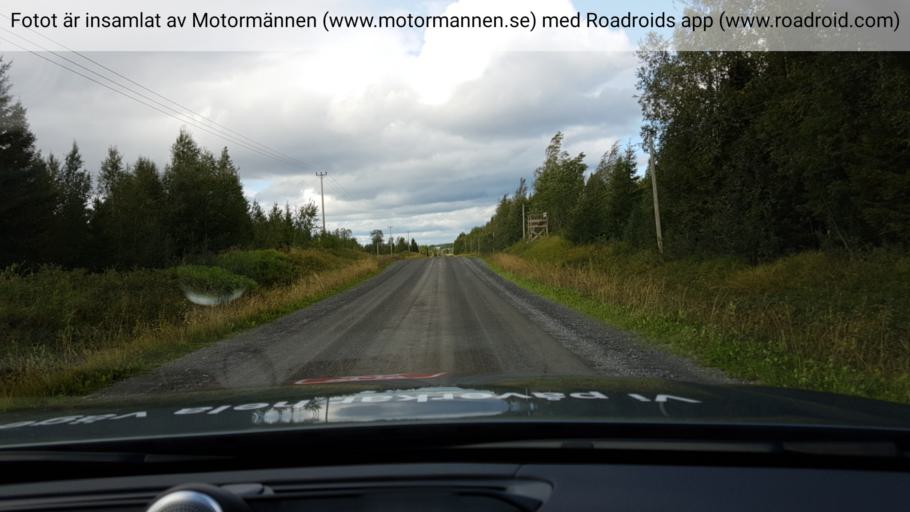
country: SE
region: Jaemtland
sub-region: OEstersunds Kommun
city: Lit
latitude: 63.6271
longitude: 14.9730
